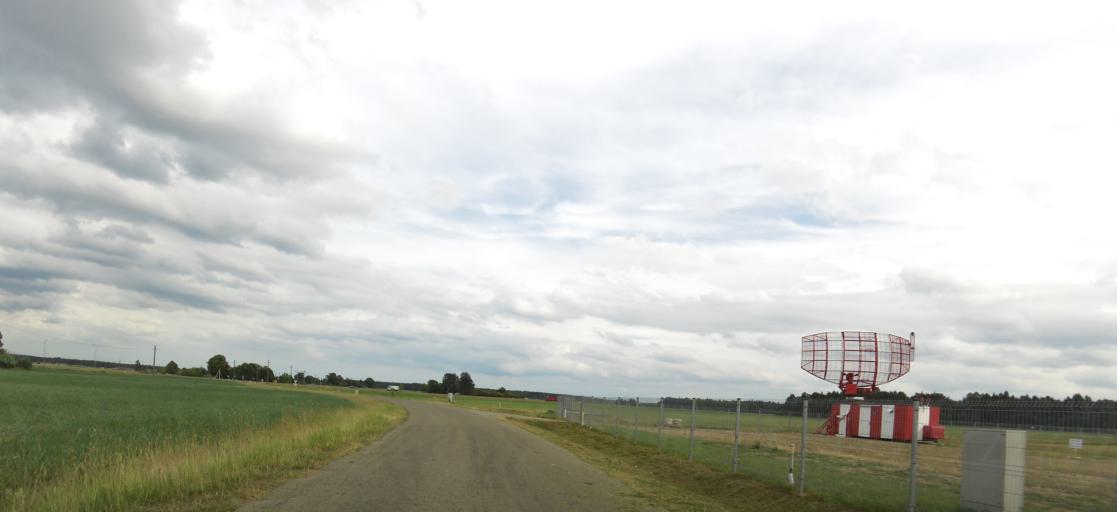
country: LT
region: Panevezys
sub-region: Panevezys City
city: Panevezys
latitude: 55.8283
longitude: 24.3613
